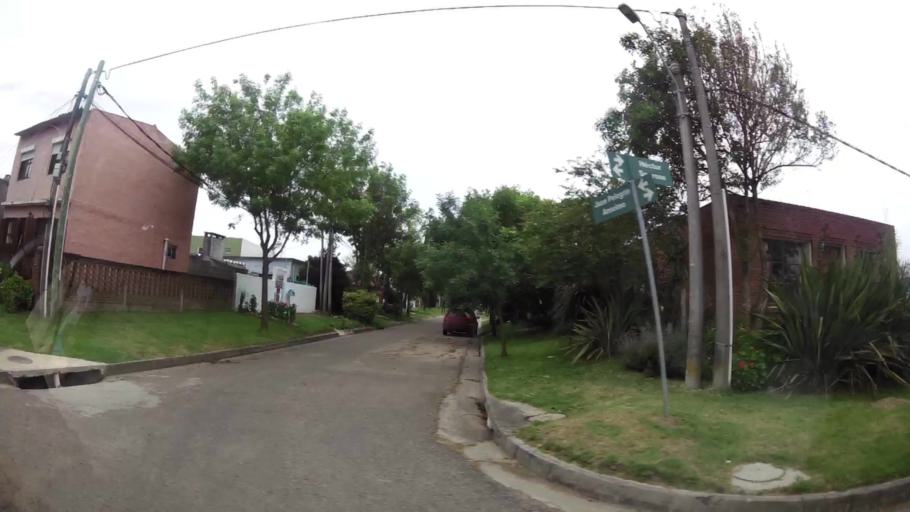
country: UY
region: Maldonado
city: Maldonado
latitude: -34.8901
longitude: -54.9502
